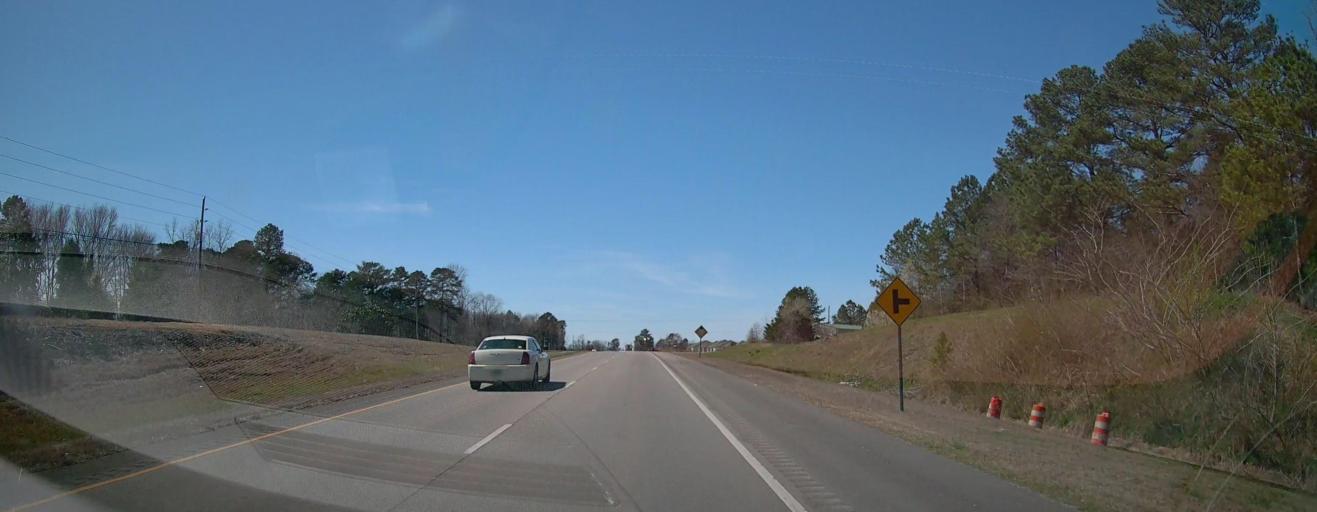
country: US
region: Alabama
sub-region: Cullman County
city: Cullman
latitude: 34.1774
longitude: -86.7313
